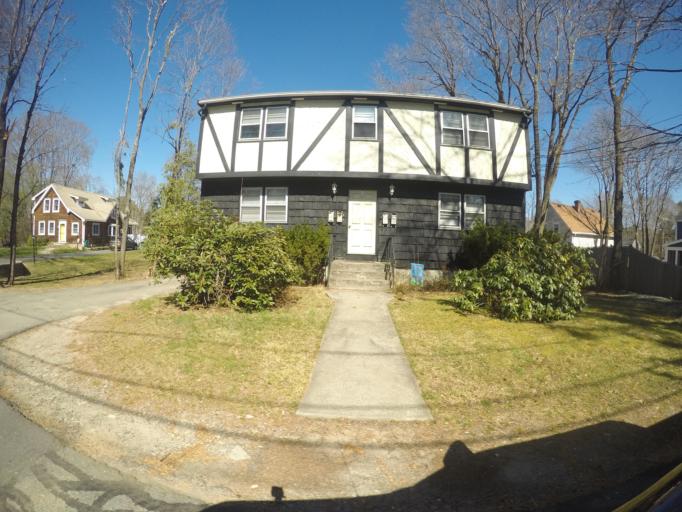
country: US
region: Massachusetts
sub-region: Norfolk County
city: Stoughton
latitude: 42.0729
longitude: -71.1023
